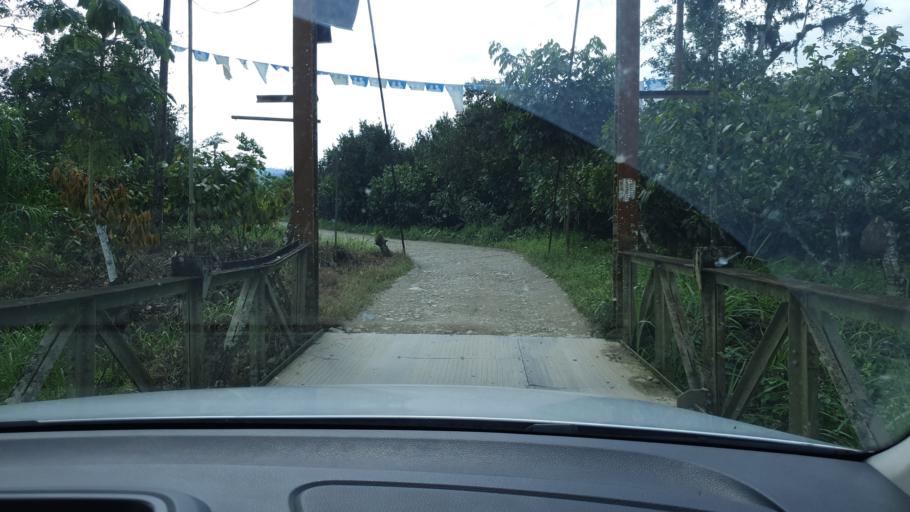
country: EC
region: Guayas
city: Naranjal
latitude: -2.8175
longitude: -79.6513
